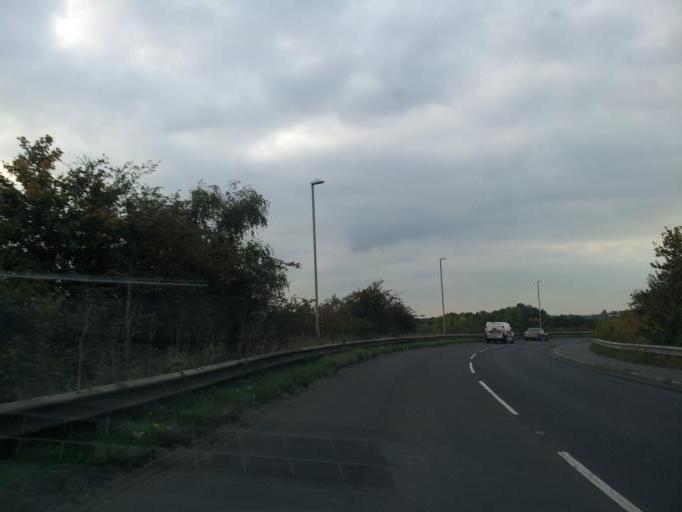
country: GB
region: England
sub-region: Nottinghamshire
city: Newark on Trent
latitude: 53.0469
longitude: -0.7787
